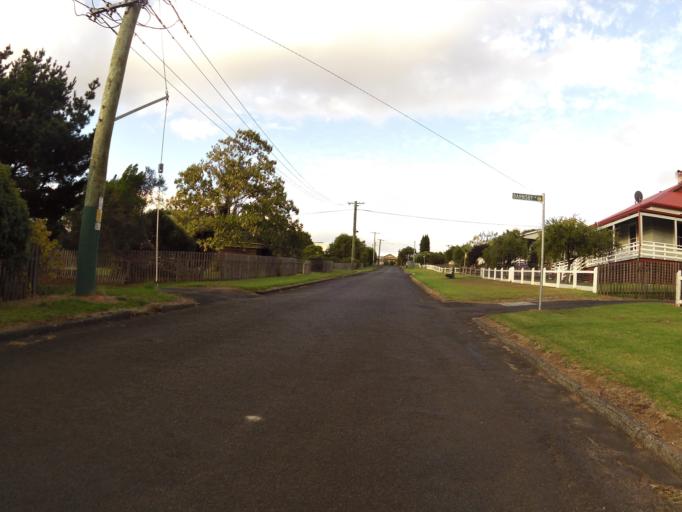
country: AU
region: Western Australia
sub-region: Manjimup
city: Pemberton
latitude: -34.4478
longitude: 116.0328
